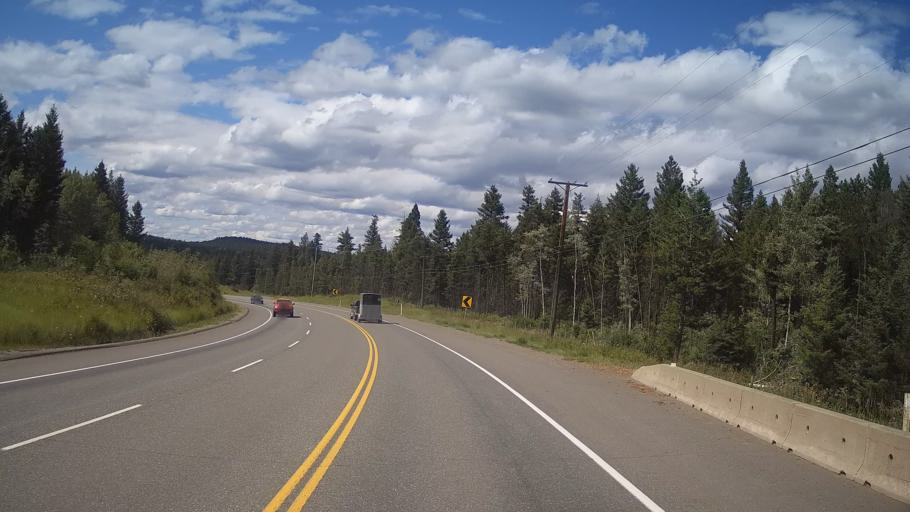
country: CA
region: British Columbia
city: Williams Lake
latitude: 51.7462
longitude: -121.3309
